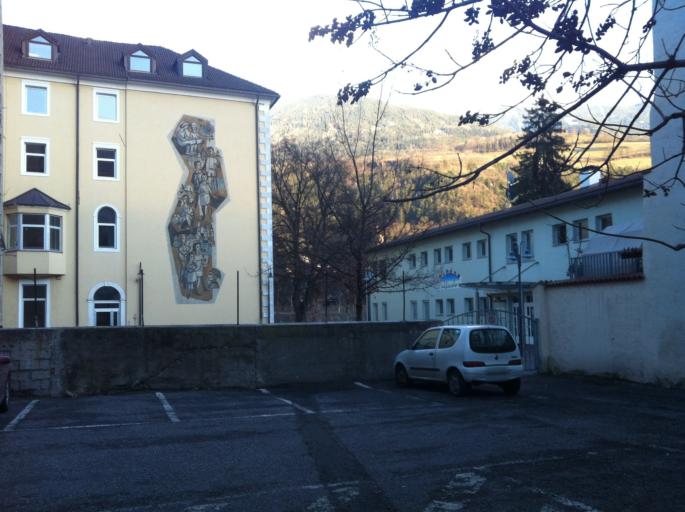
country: IT
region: Trentino-Alto Adige
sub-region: Bolzano
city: Bressanone
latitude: 46.7136
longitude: 11.6592
